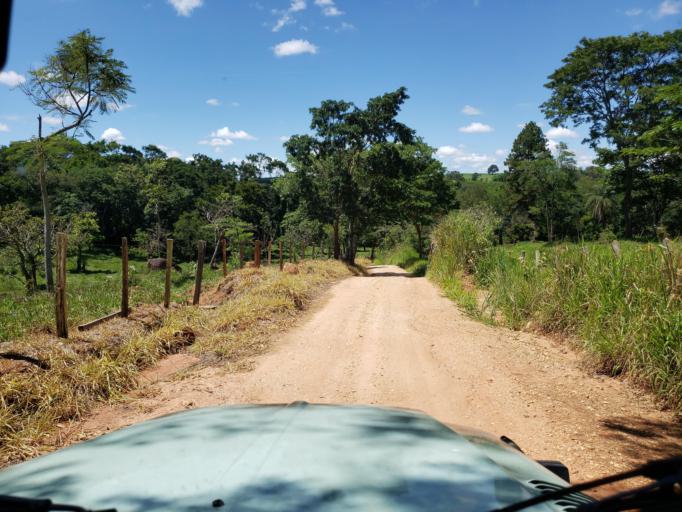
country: BR
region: Sao Paulo
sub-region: Moji-Guacu
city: Mogi-Gaucu
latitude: -22.3100
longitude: -46.8776
